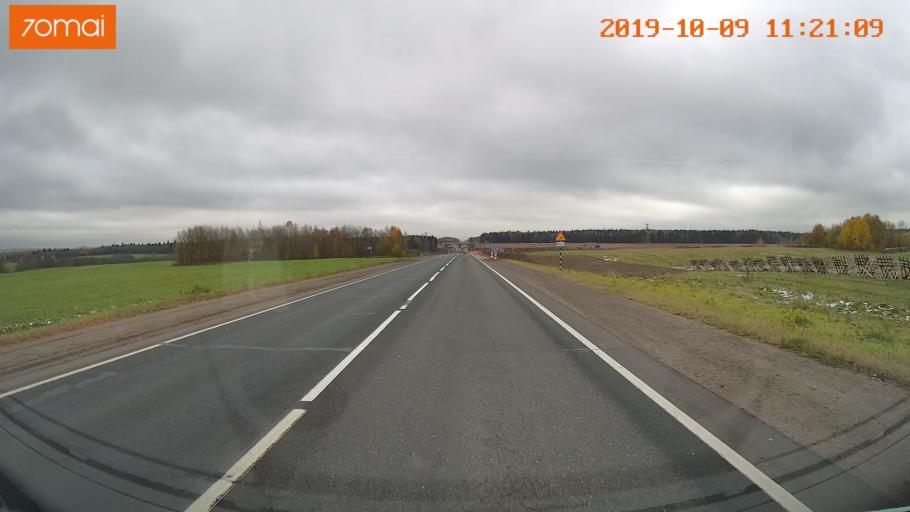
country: RU
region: Vologda
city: Vologda
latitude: 59.1420
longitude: 39.9468
